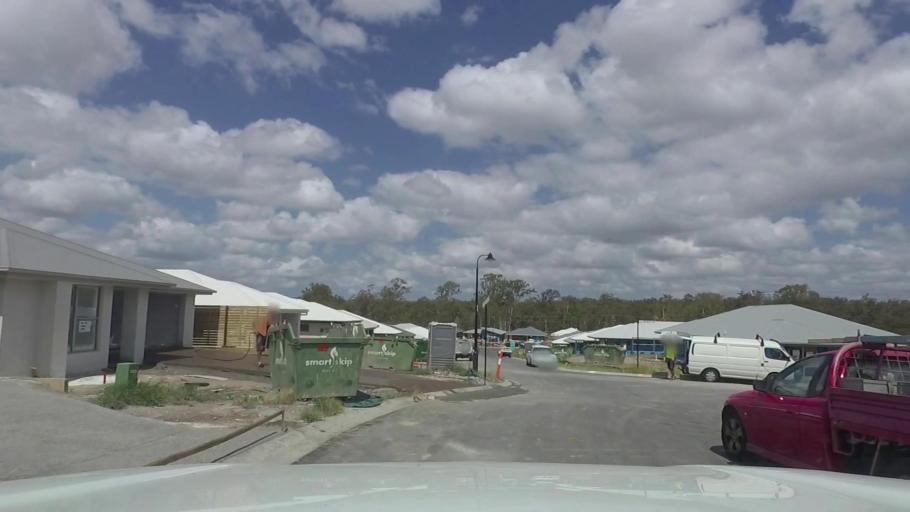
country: AU
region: Queensland
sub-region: Logan
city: Logan Reserve
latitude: -27.7197
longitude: 153.0889
